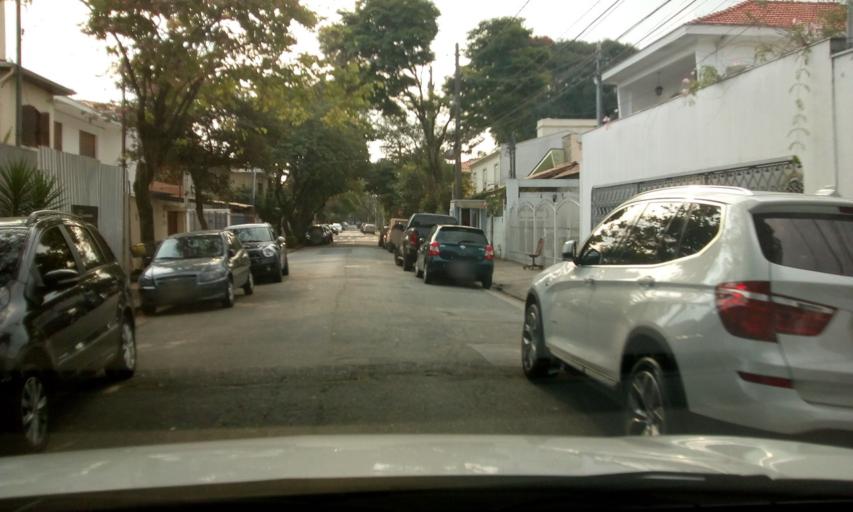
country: BR
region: Sao Paulo
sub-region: Sao Paulo
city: Sao Paulo
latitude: -23.6090
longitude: -46.6716
